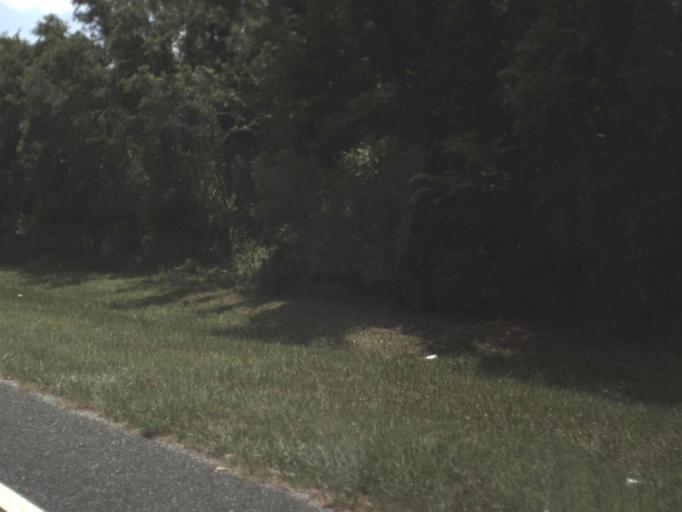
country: US
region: Florida
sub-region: Dixie County
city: Cross City
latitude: 29.6444
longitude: -83.1507
